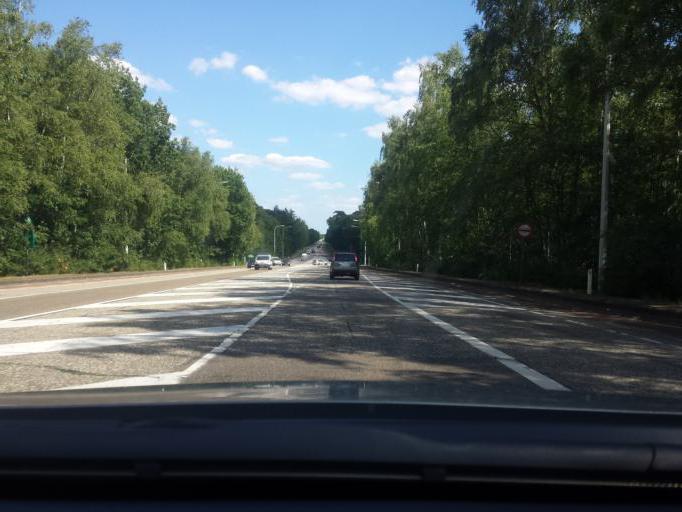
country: BE
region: Flanders
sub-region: Provincie Limburg
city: Heusden
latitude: 51.0086
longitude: 5.3069
